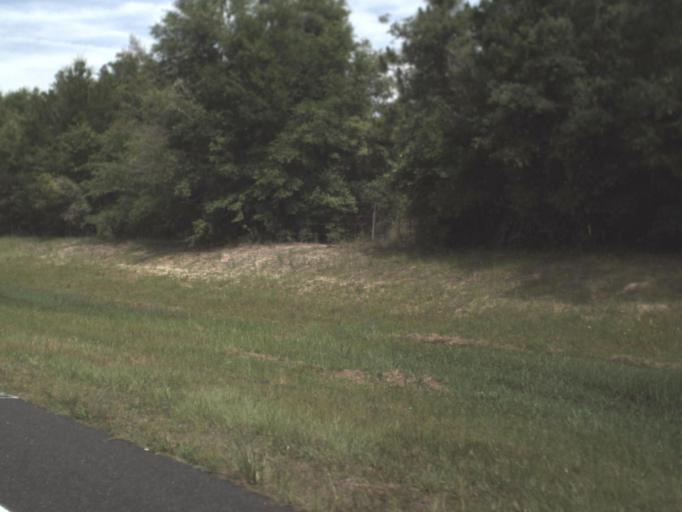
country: US
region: Florida
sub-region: Alachua County
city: Gainesville
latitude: 29.6048
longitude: -82.2158
